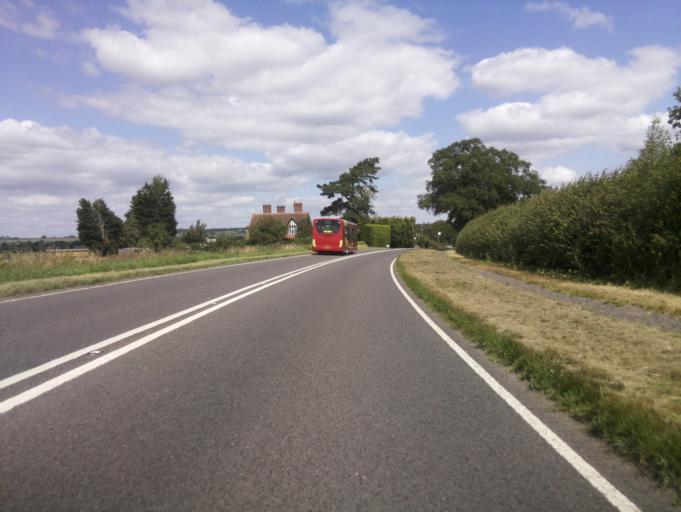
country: GB
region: England
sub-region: Buckinghamshire
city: Aylesbury
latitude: 51.8570
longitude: -0.8300
